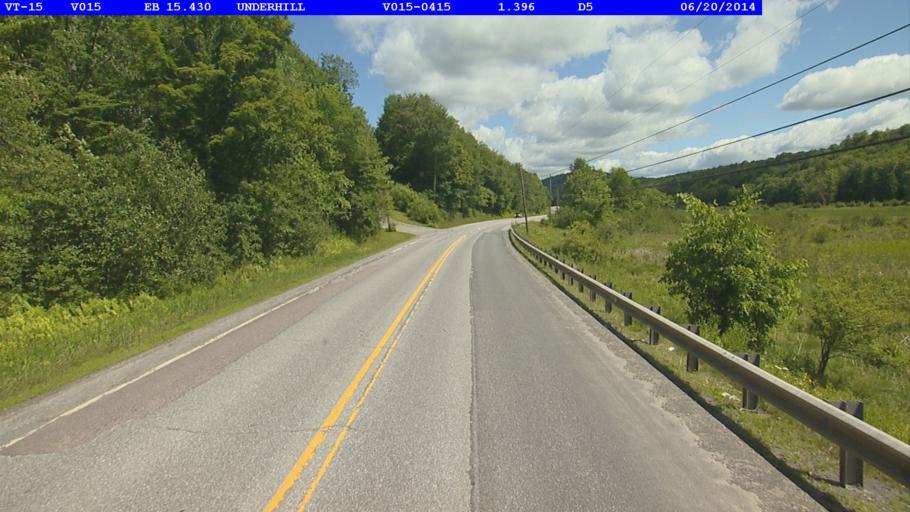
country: US
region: Vermont
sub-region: Chittenden County
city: Jericho
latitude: 44.5445
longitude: -72.9485
